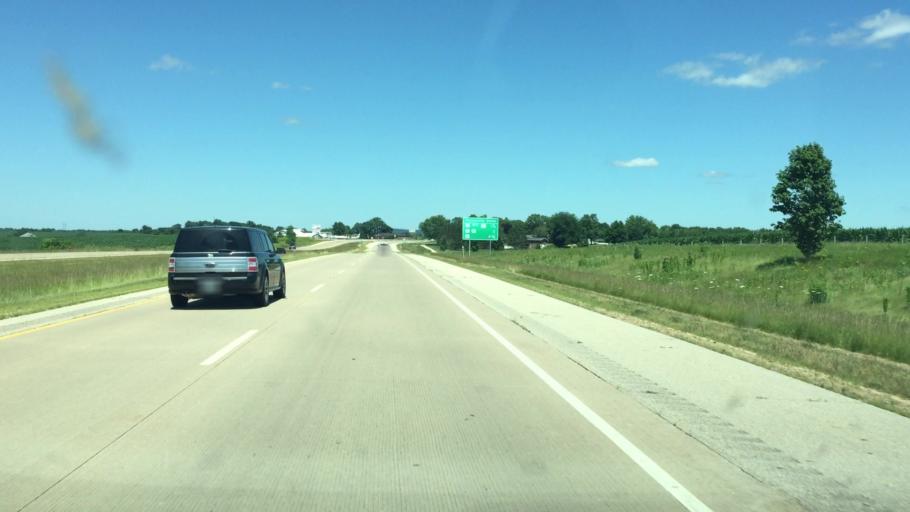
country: US
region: Wisconsin
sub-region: Grant County
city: Platteville
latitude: 42.7065
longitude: -90.5207
